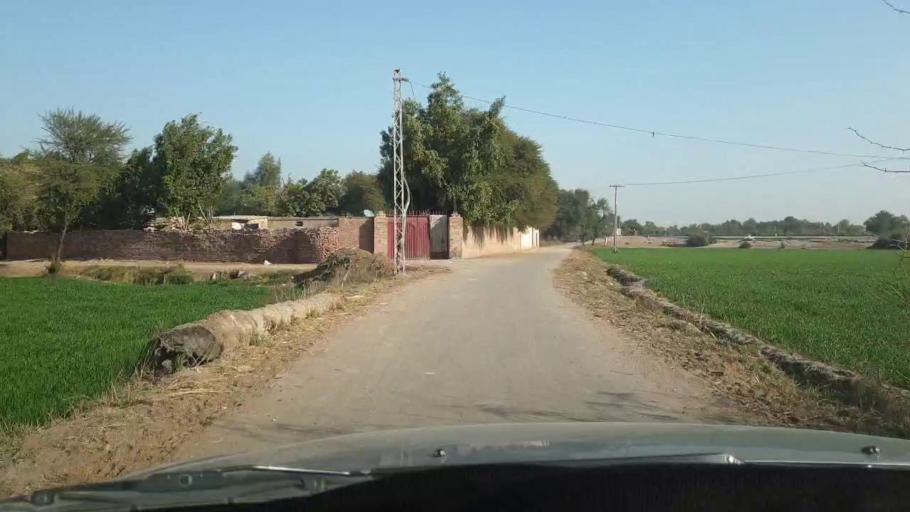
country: PK
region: Sindh
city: Mirpur Mathelo
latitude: 28.0202
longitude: 69.5832
